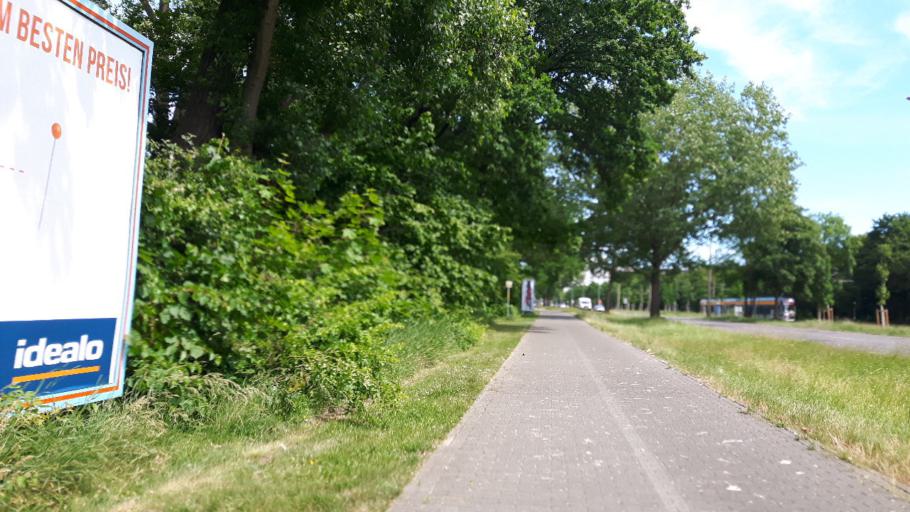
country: DE
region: Saxony
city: Markranstadt
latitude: 51.3202
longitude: 12.2812
